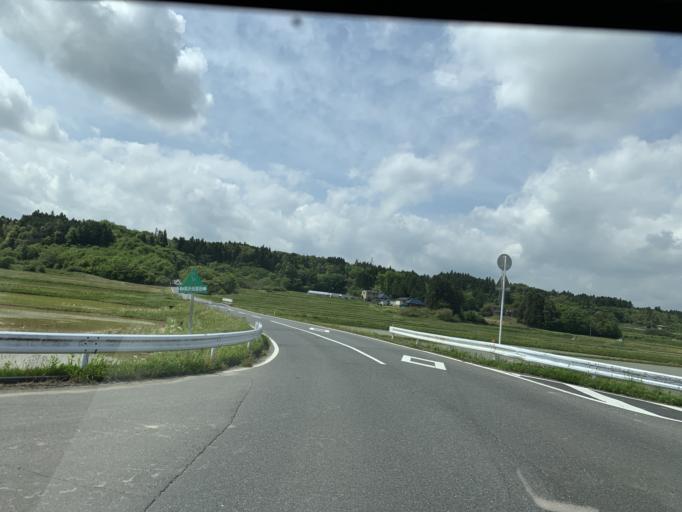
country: JP
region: Iwate
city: Ichinoseki
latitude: 38.7816
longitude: 140.9985
